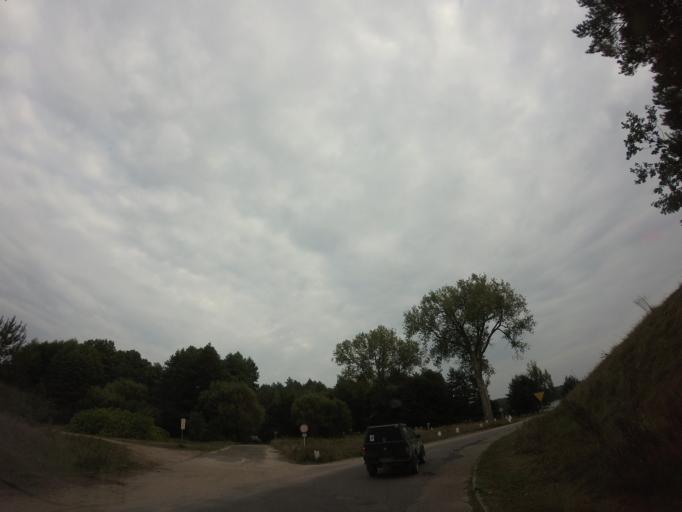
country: PL
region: West Pomeranian Voivodeship
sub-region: Powiat drawski
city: Drawsko Pomorskie
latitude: 53.4760
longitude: 15.7723
